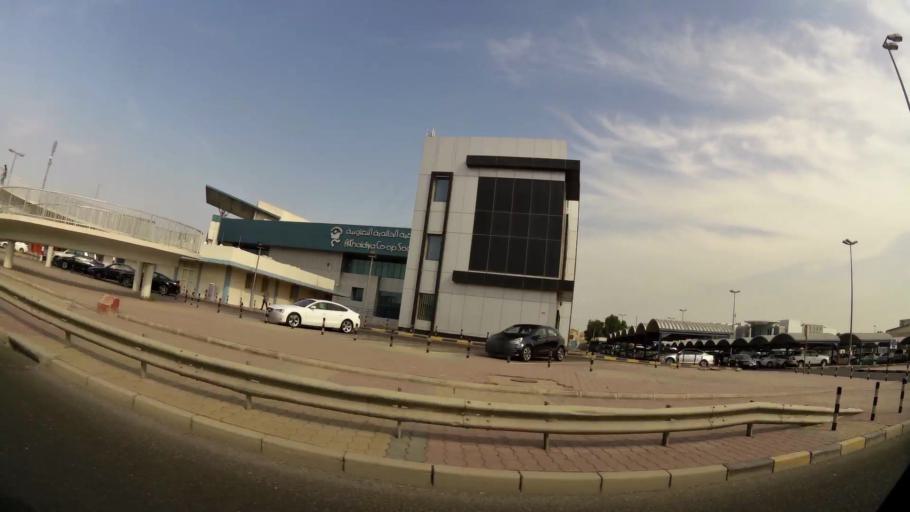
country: KW
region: Al Asimah
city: Ash Shamiyah
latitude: 29.3283
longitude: 47.9620
